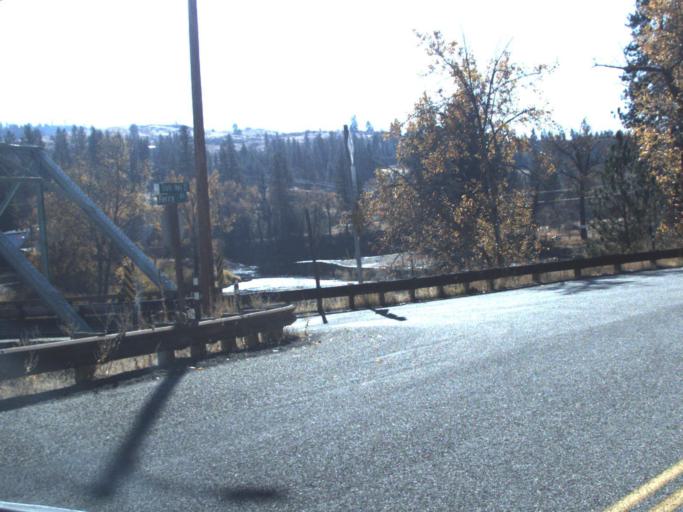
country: CA
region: British Columbia
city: Grand Forks
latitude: 48.8856
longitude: -118.6019
